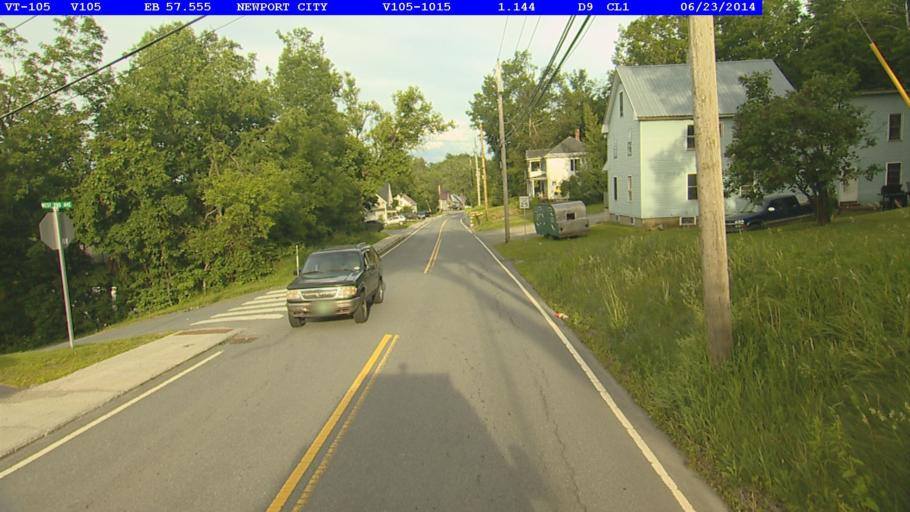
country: US
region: Vermont
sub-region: Orleans County
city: Newport
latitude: 44.9324
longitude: -72.2212
